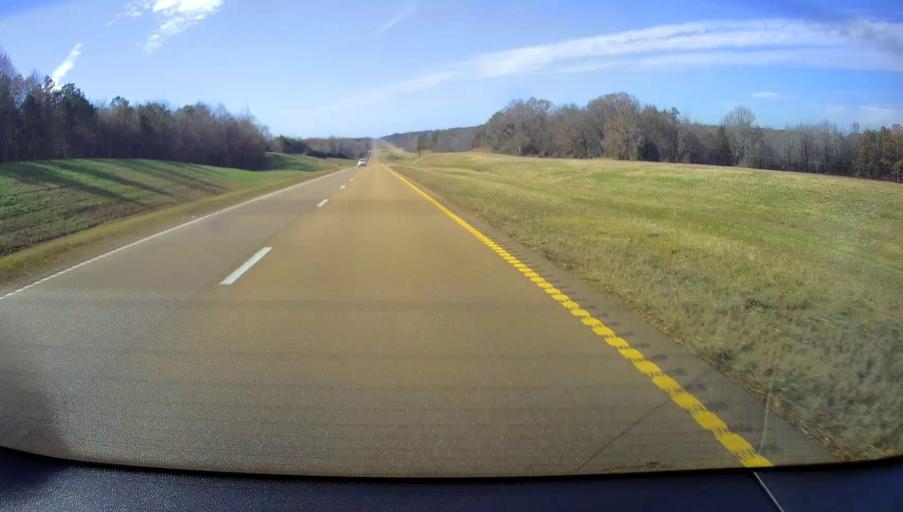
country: US
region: Mississippi
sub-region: Benton County
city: Ashland
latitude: 34.9532
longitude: -89.0447
